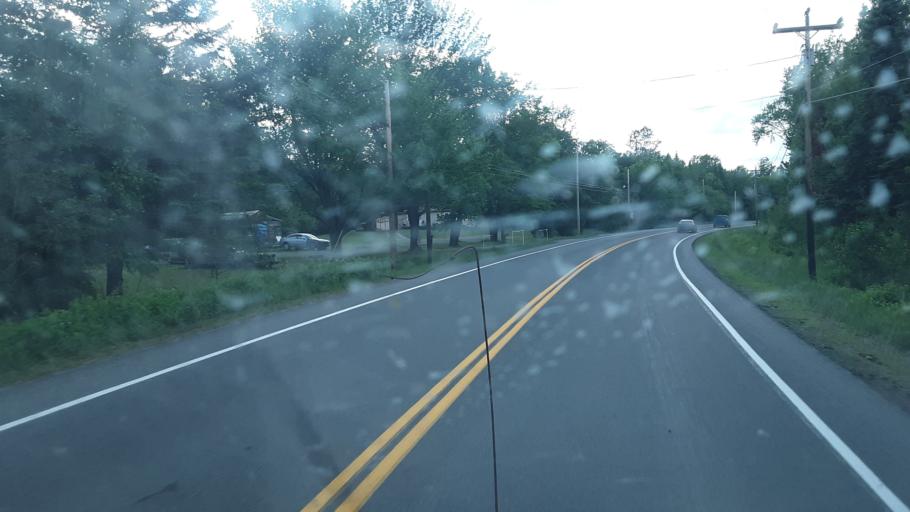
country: US
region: Maine
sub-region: Penobscot County
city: Patten
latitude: 45.9289
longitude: -68.4459
